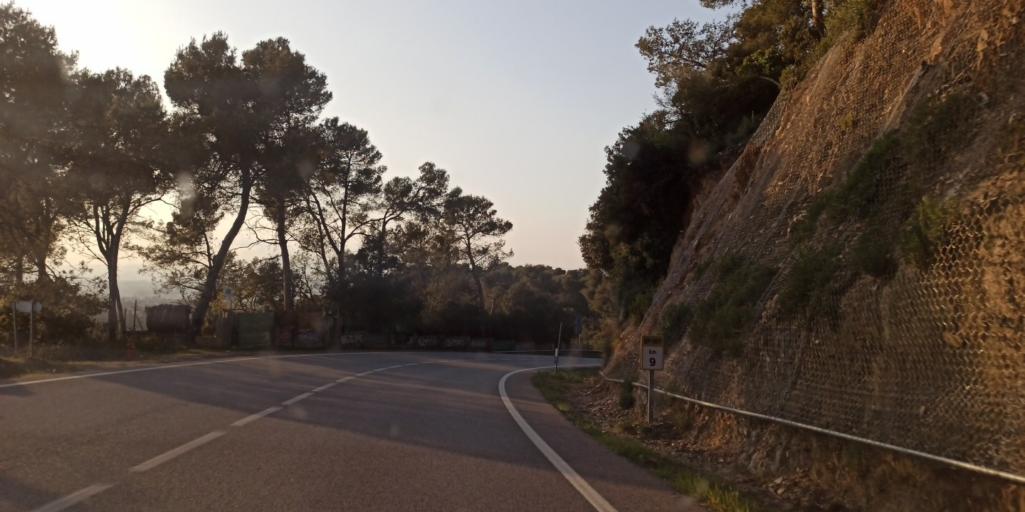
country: ES
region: Catalonia
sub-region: Provincia de Barcelona
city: Sant Cugat del Valles
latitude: 41.4470
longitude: 2.0947
